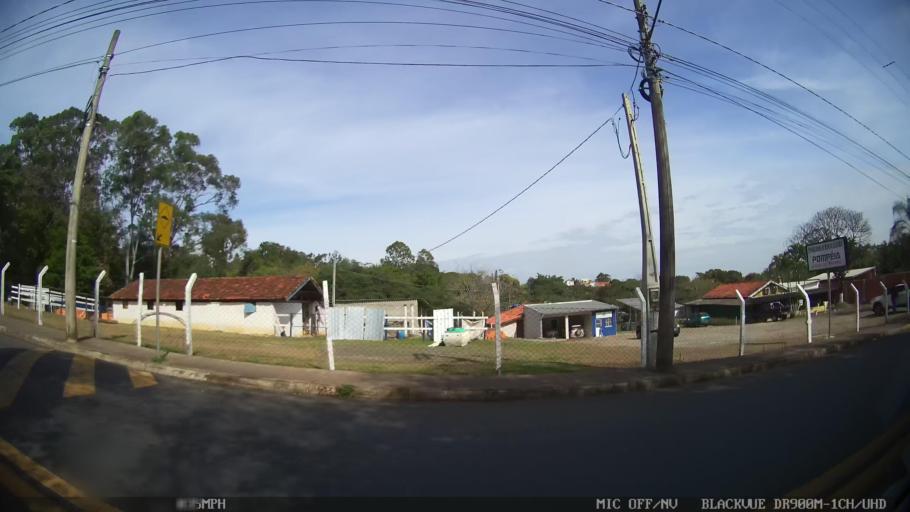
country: BR
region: Sao Paulo
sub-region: Piracicaba
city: Piracicaba
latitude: -22.7582
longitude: -47.6041
